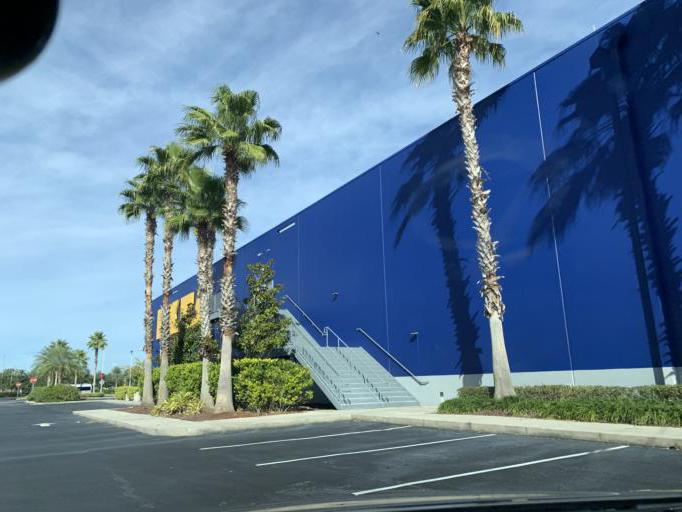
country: US
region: Florida
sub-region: Orange County
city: Oak Ridge
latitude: 28.4825
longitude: -81.4286
